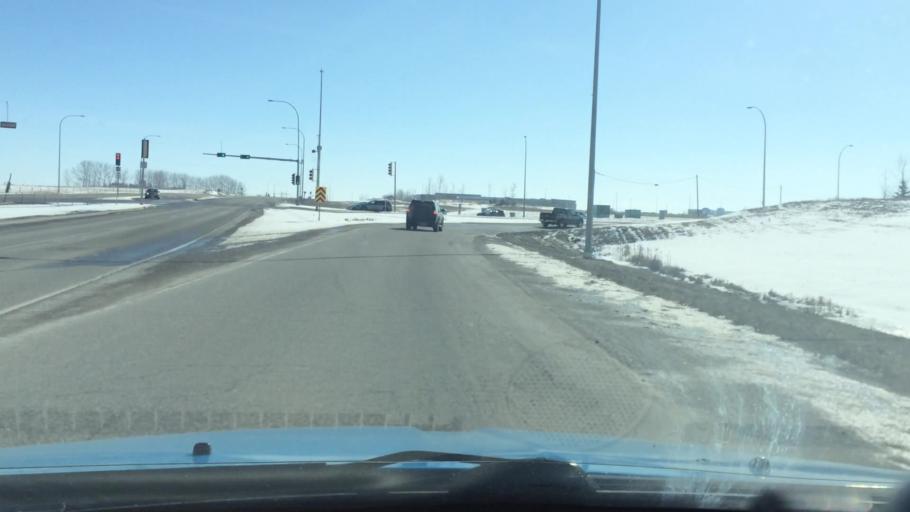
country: CA
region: Alberta
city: Airdrie
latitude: 51.2122
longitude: -113.9922
